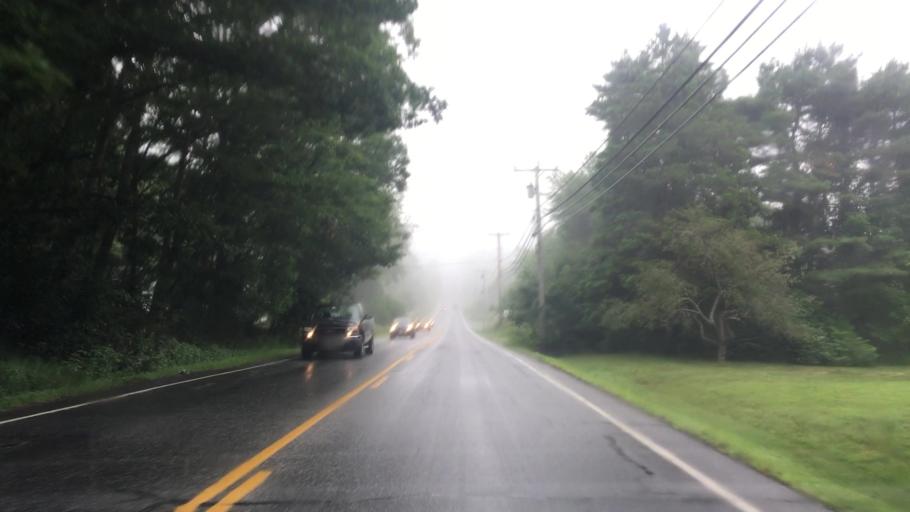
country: US
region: Maine
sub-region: Lincoln County
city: Boothbay
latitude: 43.8732
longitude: -69.6328
